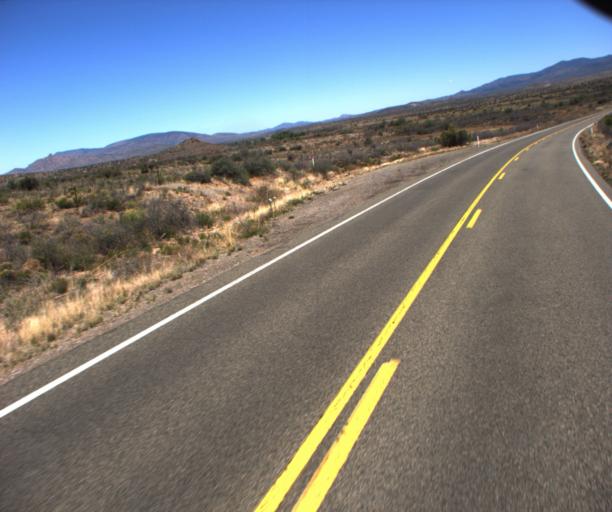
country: US
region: Arizona
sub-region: Yavapai County
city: Congress
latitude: 34.3494
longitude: -112.6822
